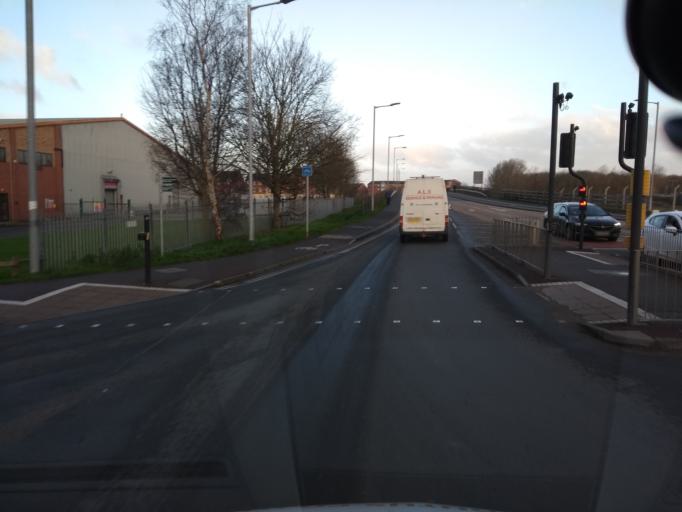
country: GB
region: England
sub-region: Somerset
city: Bridgwater
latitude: 51.1370
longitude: -2.9996
